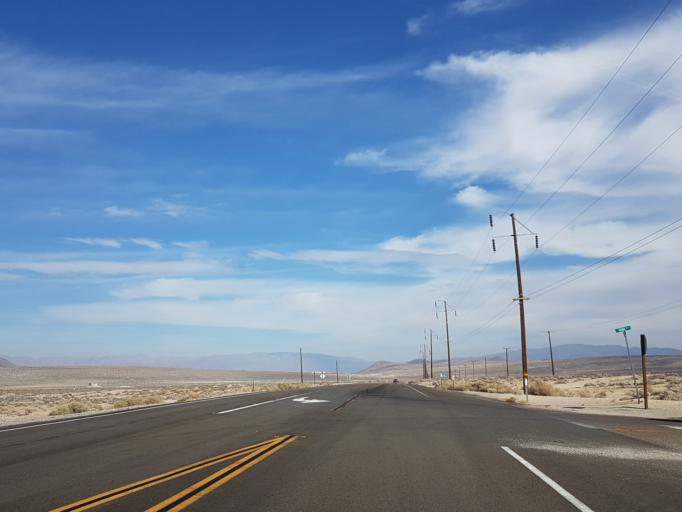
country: US
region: California
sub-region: San Bernardino County
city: Searles Valley
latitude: 35.6470
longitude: -117.5107
